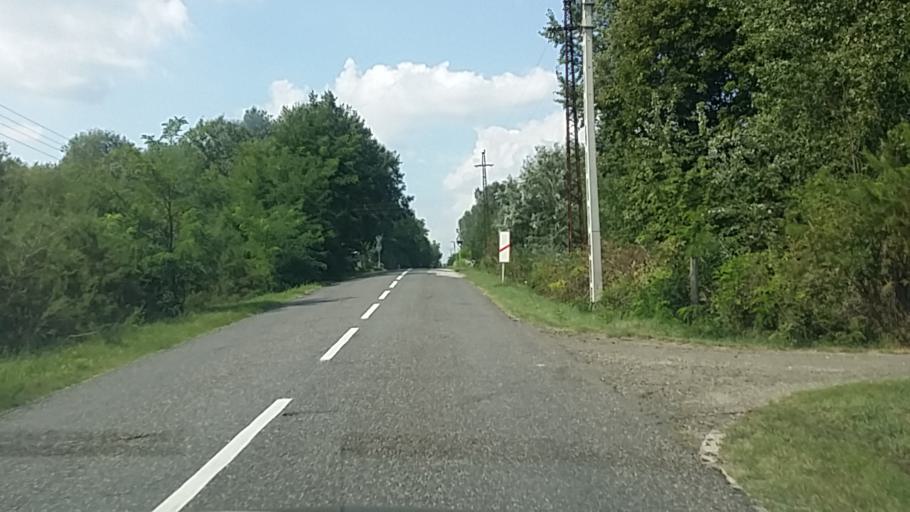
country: HU
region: Bacs-Kiskun
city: Lakitelek
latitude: 46.8595
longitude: 19.9780
